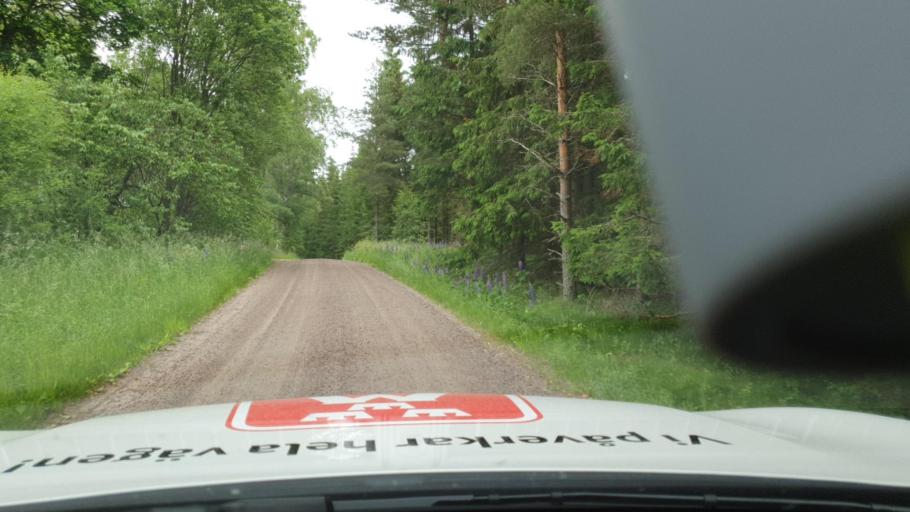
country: SE
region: Vaestra Goetaland
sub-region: Hjo Kommun
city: Hjo
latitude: 58.3897
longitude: 14.3430
